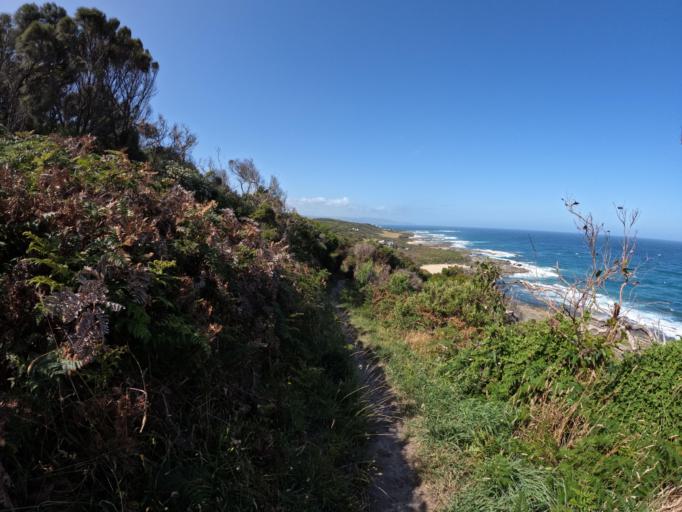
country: AU
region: Victoria
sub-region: Colac-Otway
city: Apollo Bay
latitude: -38.7899
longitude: 143.6473
